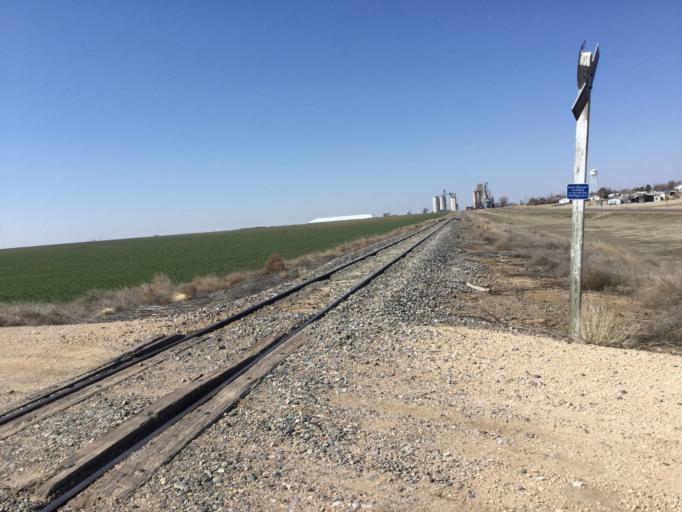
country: US
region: Kansas
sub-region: Stanton County
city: Johnson
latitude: 37.5269
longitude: -101.8709
